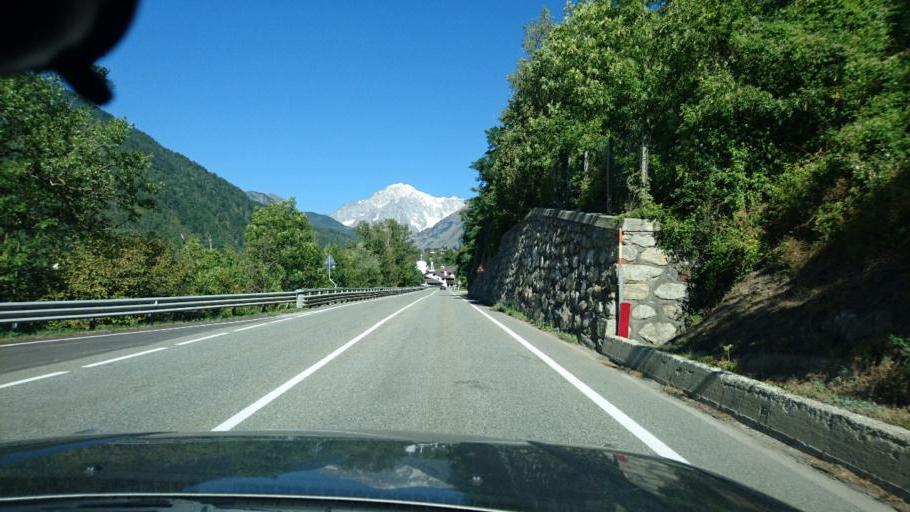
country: IT
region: Aosta Valley
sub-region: Valle d'Aosta
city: La Salle
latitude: 45.7267
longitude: 7.0928
